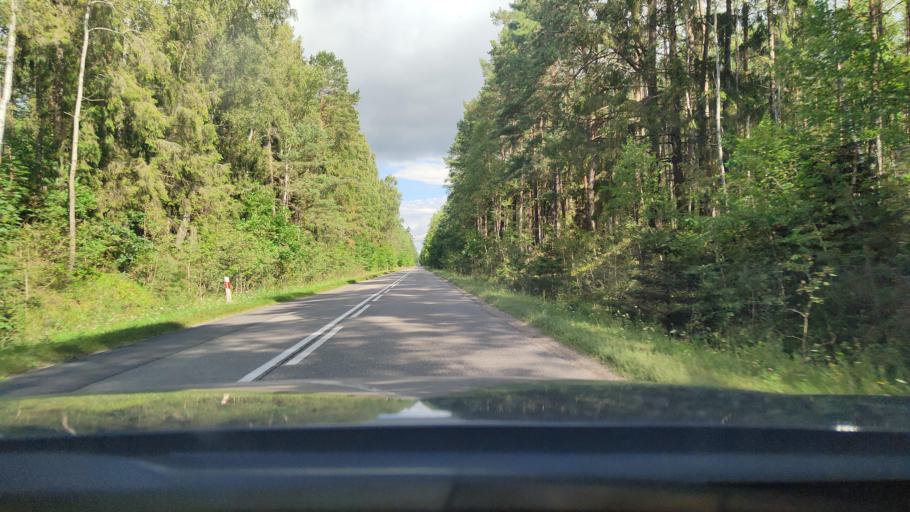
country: PL
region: Pomeranian Voivodeship
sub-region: Powiat wejherowski
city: Orle
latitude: 54.6585
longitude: 18.2087
